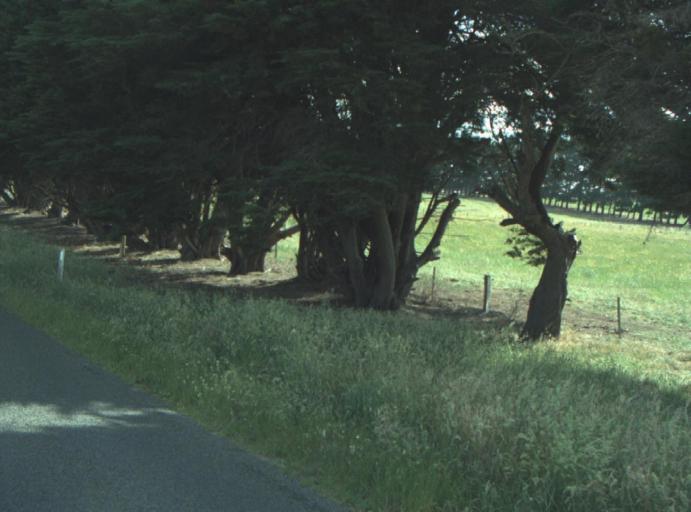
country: AU
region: Victoria
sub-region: Greater Geelong
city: Leopold
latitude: -38.1964
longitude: 144.5100
